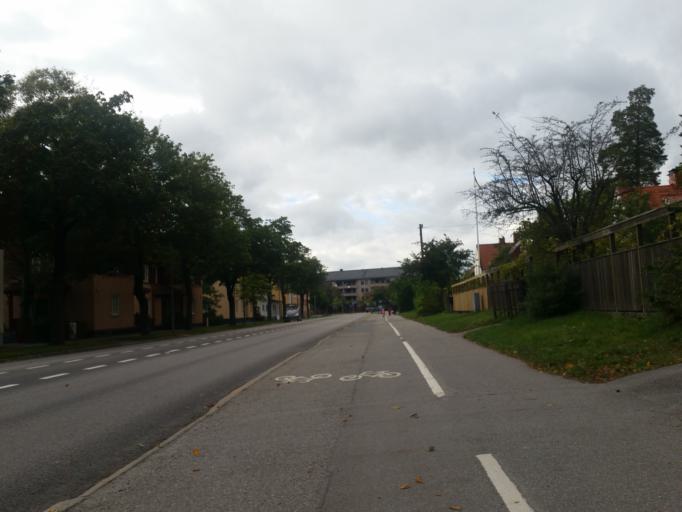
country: SE
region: Stockholm
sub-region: Stockholms Kommun
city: Arsta
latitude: 59.2833
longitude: 18.1014
